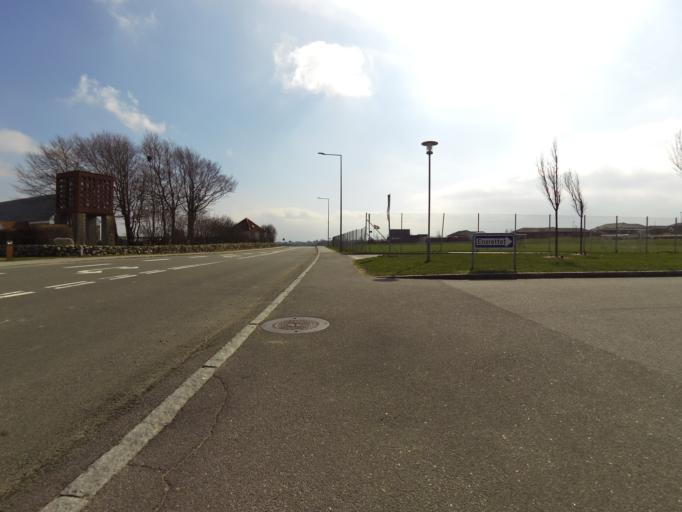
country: DK
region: Central Jutland
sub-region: Struer Kommune
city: Struer
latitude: 56.4761
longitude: 8.6050
